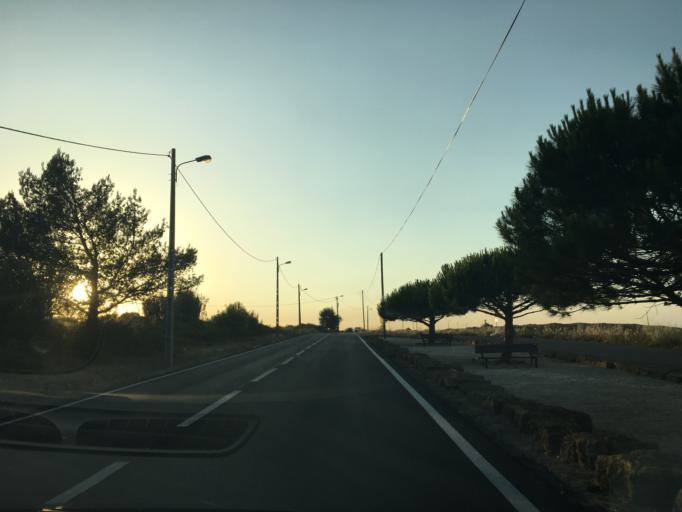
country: PT
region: Lisbon
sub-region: Sintra
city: Sintra
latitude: 38.8245
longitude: -9.4102
